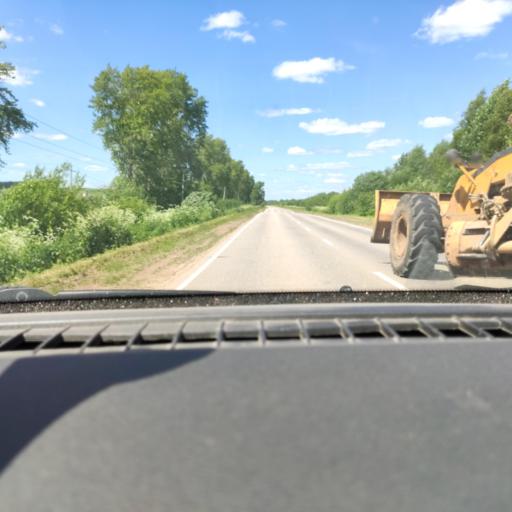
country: RU
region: Perm
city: Chaykovskaya
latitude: 58.0991
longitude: 55.5931
